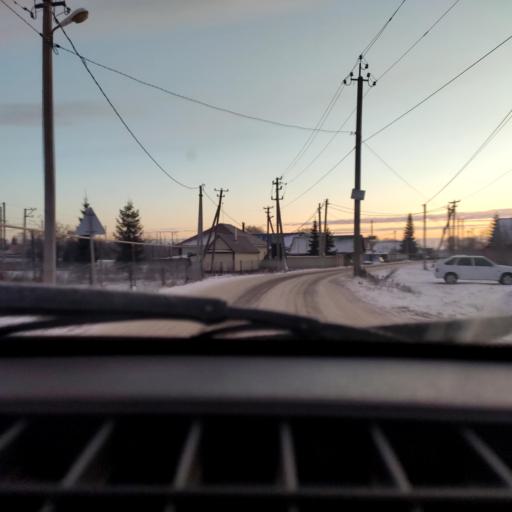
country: RU
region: Bashkortostan
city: Avdon
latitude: 54.6499
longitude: 55.7715
